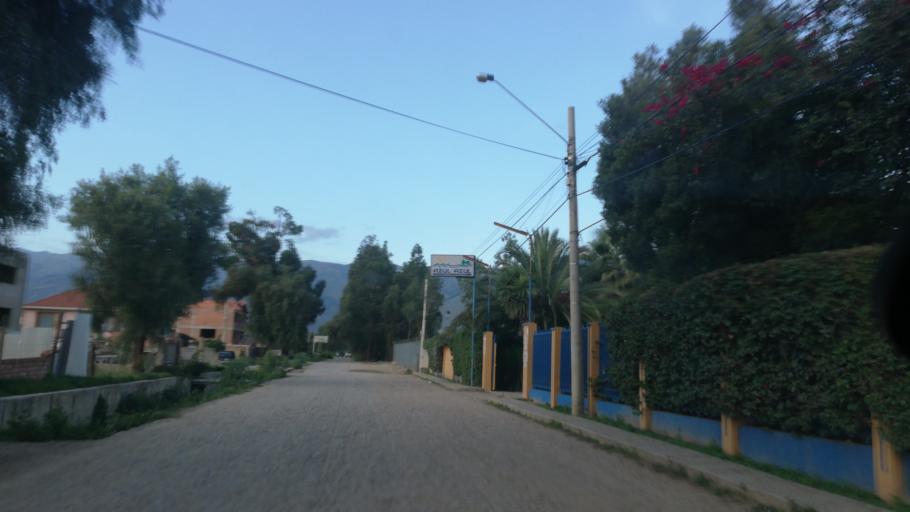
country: BO
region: Cochabamba
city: Cochabamba
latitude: -17.3787
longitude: -66.2074
